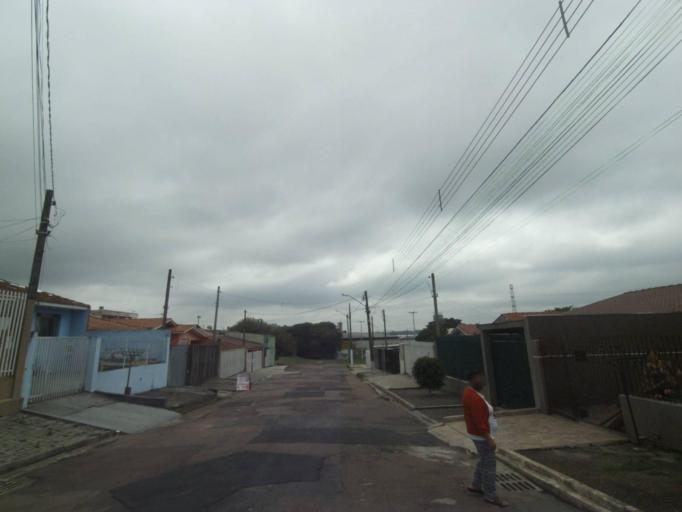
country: BR
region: Parana
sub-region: Curitiba
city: Curitiba
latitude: -25.4804
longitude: -49.3523
